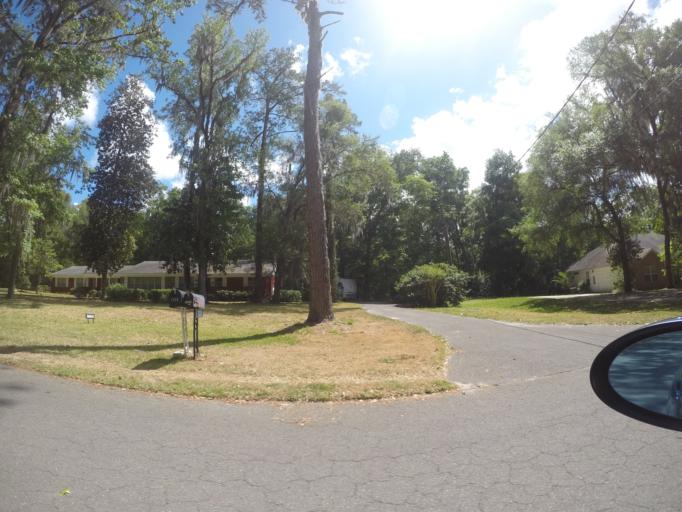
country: US
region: Florida
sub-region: Alachua County
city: Gainesville
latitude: 29.6340
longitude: -82.3311
